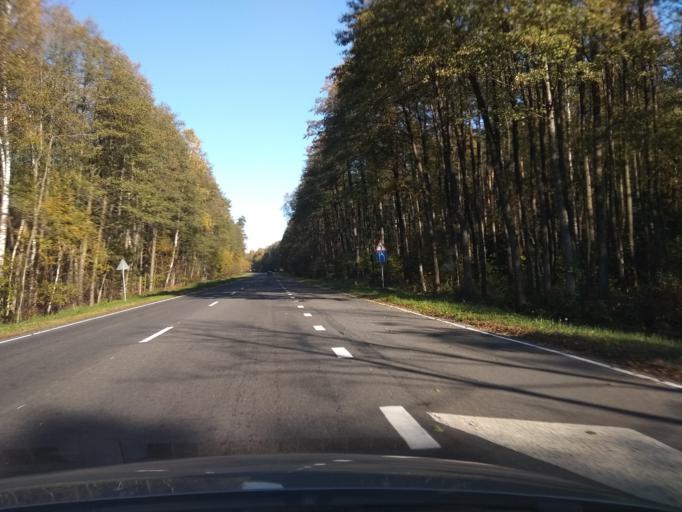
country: BY
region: Brest
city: Kobryn
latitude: 52.0621
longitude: 24.2829
